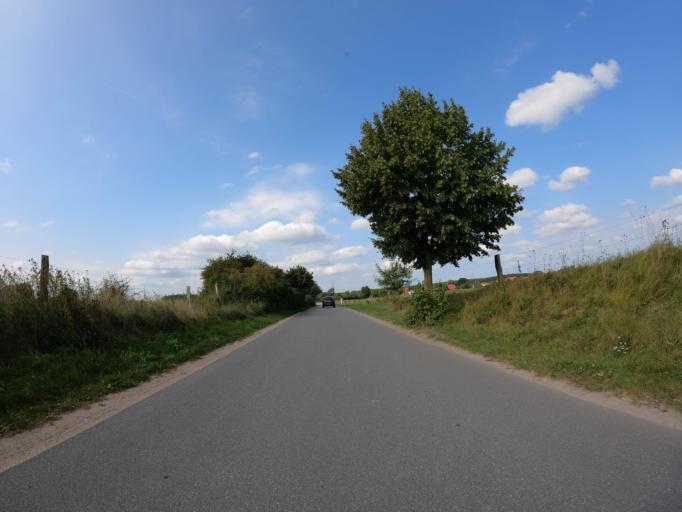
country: DE
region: Mecklenburg-Vorpommern
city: Malchow
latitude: 53.5145
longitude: 12.4422
